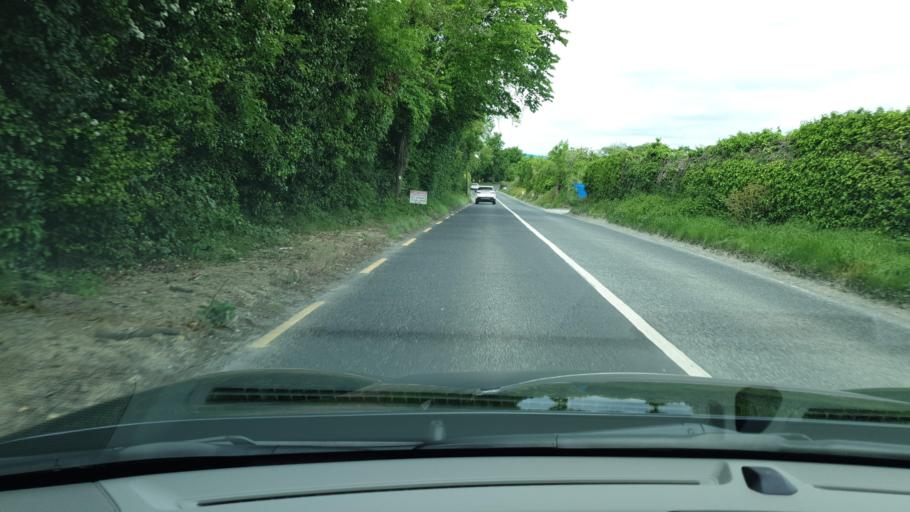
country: IE
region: Leinster
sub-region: Fingal County
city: Swords
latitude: 53.4519
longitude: -6.2624
